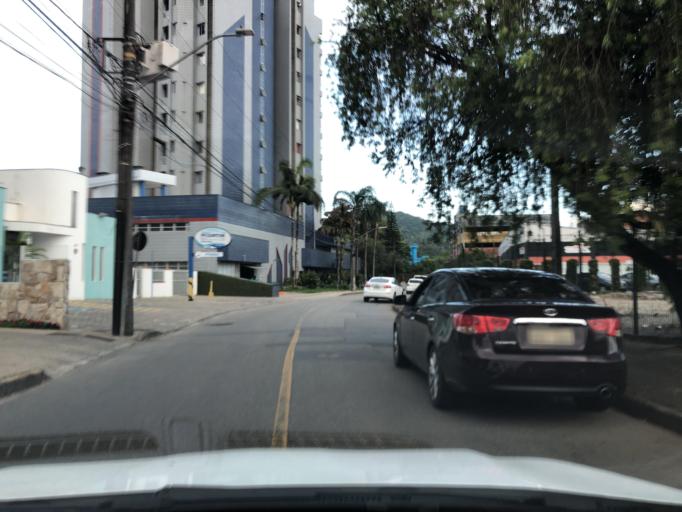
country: BR
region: Santa Catarina
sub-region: Joinville
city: Joinville
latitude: -26.2916
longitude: -48.8466
